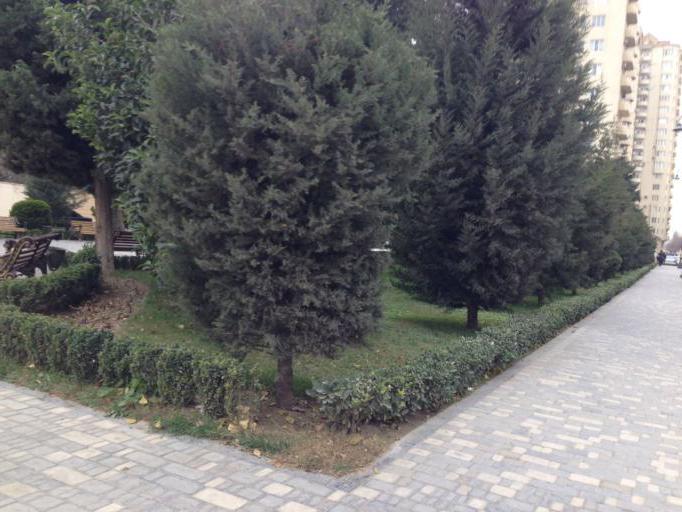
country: AZ
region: Baki
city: Baku
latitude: 40.3994
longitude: 49.8701
